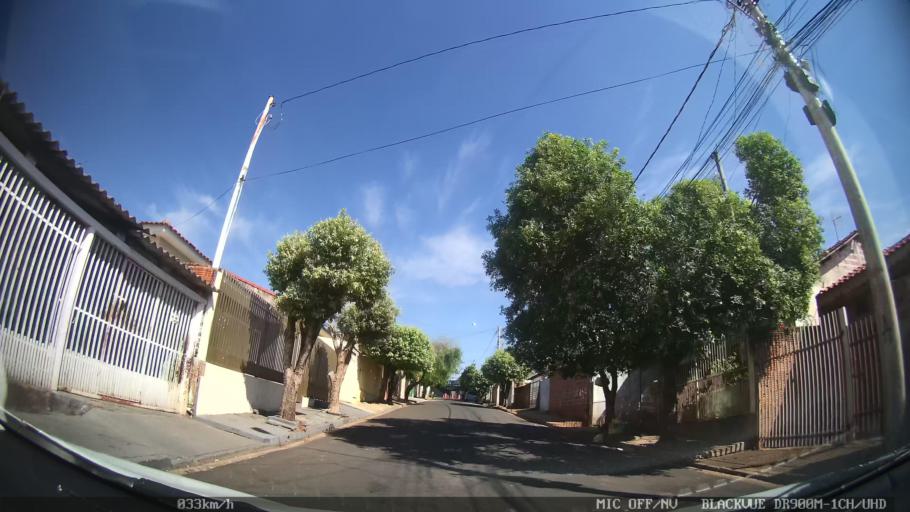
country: BR
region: Sao Paulo
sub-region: Sao Jose Do Rio Preto
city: Sao Jose do Rio Preto
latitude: -20.7748
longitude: -49.4044
